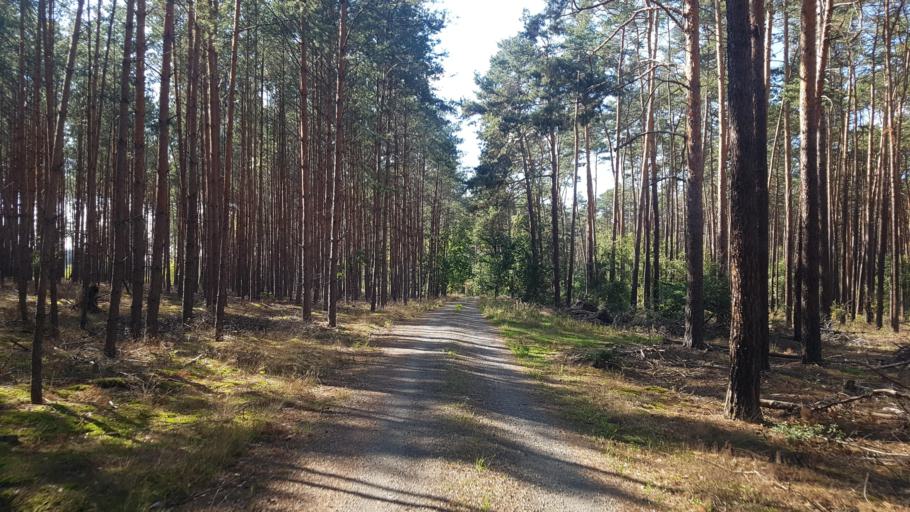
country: DE
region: Brandenburg
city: Lebusa
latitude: 51.8223
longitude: 13.4250
